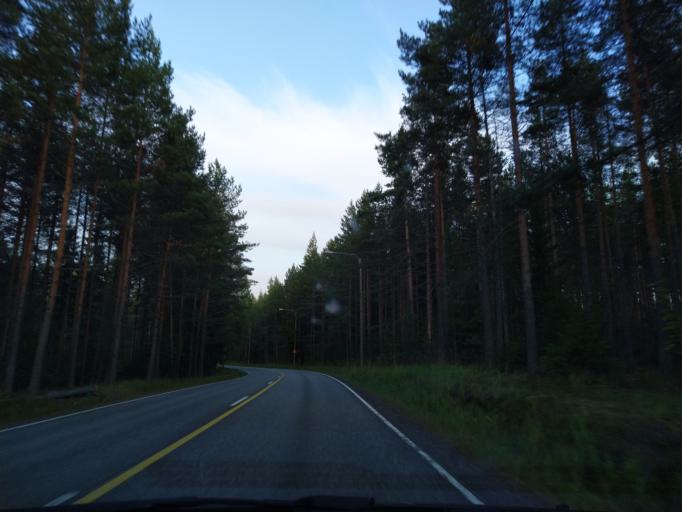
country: FI
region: Uusimaa
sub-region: Helsinki
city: Tuusula
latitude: 60.3536
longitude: 25.0161
